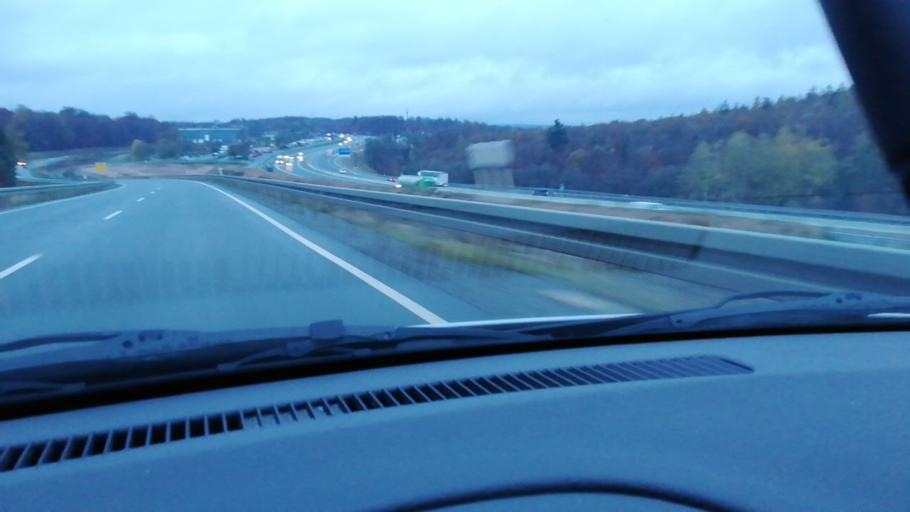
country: DE
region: Bavaria
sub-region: Regierungsbezirk Unterfranken
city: Weibersbrunn
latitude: 49.8914
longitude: 9.4015
